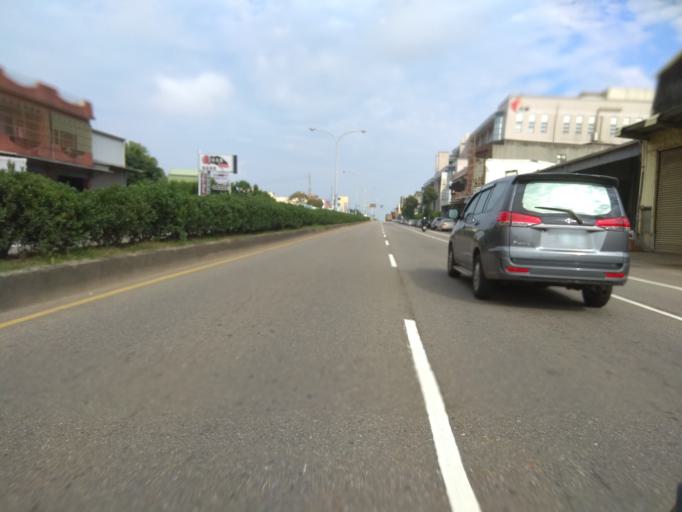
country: TW
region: Taiwan
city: Taoyuan City
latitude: 25.0549
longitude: 121.1587
